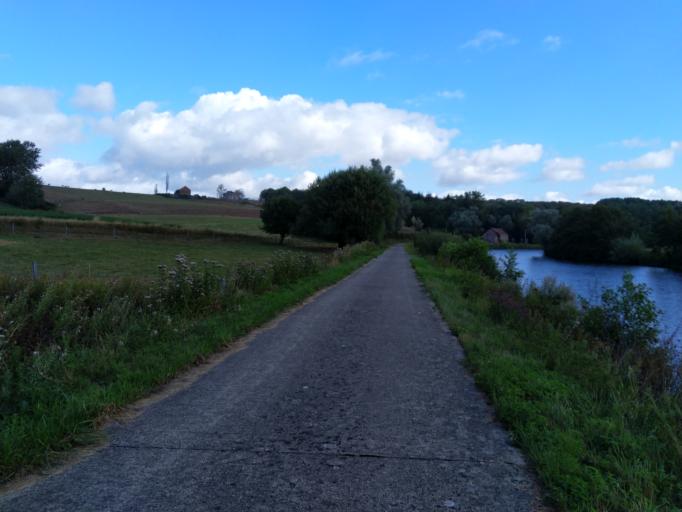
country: BE
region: Wallonia
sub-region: Province du Hainaut
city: Merbes-le-Chateau
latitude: 50.3242
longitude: 4.2098
